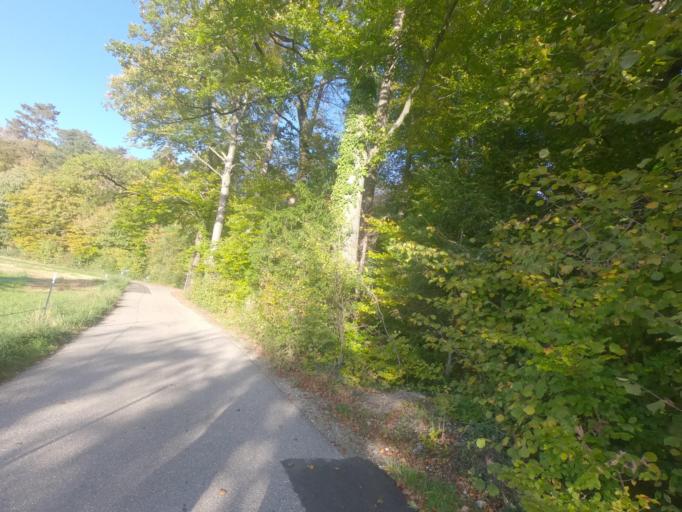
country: CH
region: Solothurn
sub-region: Bezirk Lebern
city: Langendorf
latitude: 47.2214
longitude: 7.5299
